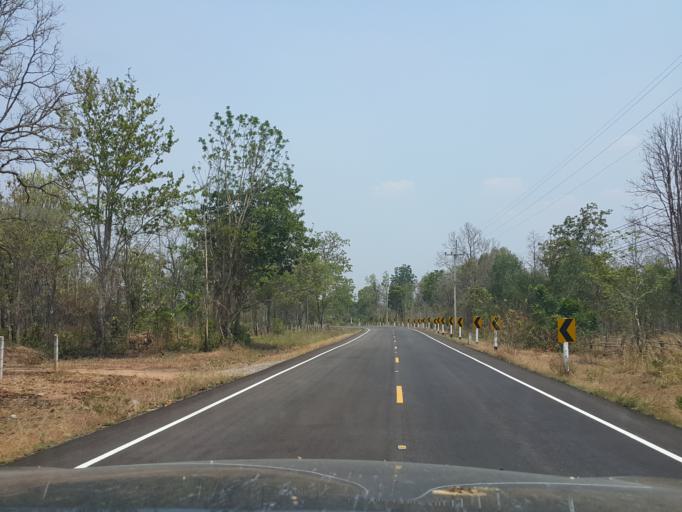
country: TH
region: Lampang
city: Mae Phrik
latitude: 17.5469
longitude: 99.1308
